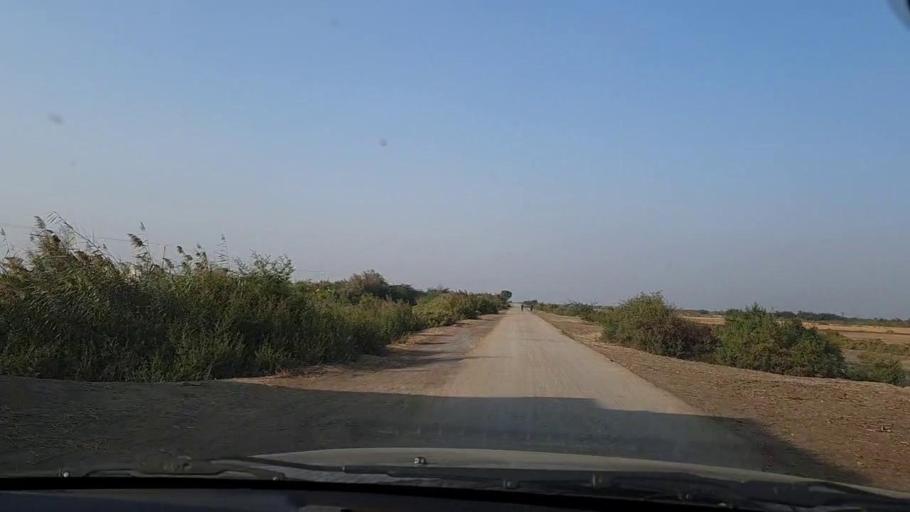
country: PK
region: Sindh
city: Chuhar Jamali
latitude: 24.3034
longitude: 67.7556
